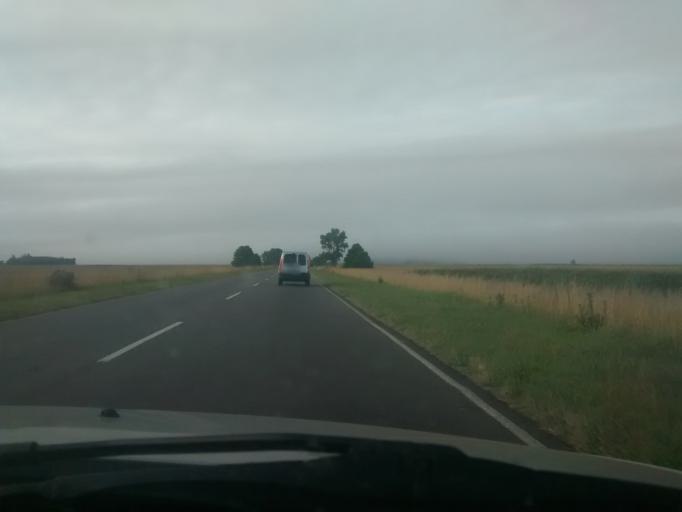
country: AR
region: Buenos Aires
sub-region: Partido de Brandsen
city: Brandsen
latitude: -35.3435
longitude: -58.2461
